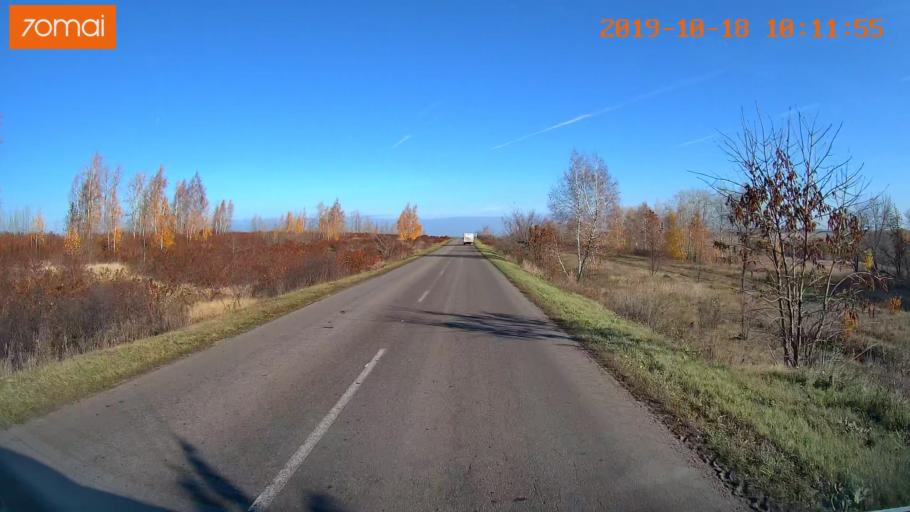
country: RU
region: Tula
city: Kurkino
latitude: 53.3877
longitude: 38.5036
